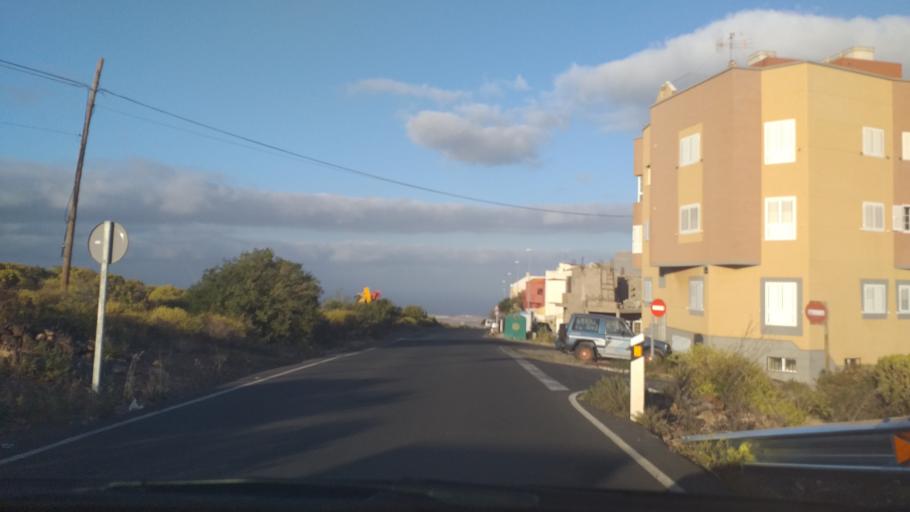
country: ES
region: Canary Islands
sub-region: Provincia de Las Palmas
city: Ingenio
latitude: 27.9216
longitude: -15.4506
